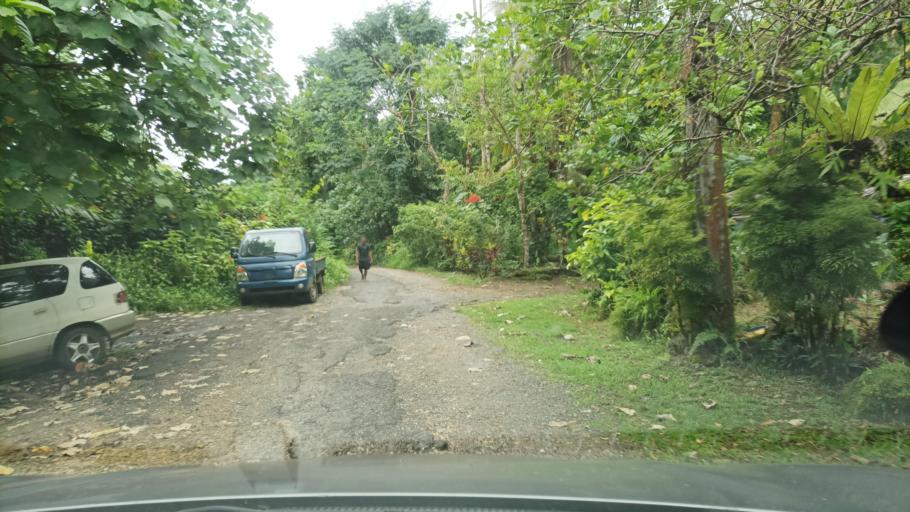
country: FM
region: Pohnpei
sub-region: Kolonia Municipality
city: Kolonia
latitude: 6.9408
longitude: 158.2705
